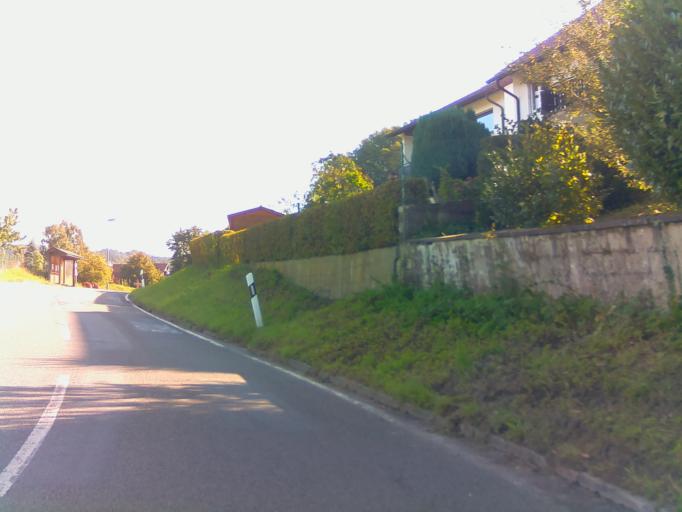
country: DE
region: Baden-Wuerttemberg
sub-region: Karlsruhe Region
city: Wilhelmsfeld
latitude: 49.5104
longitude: 8.7411
